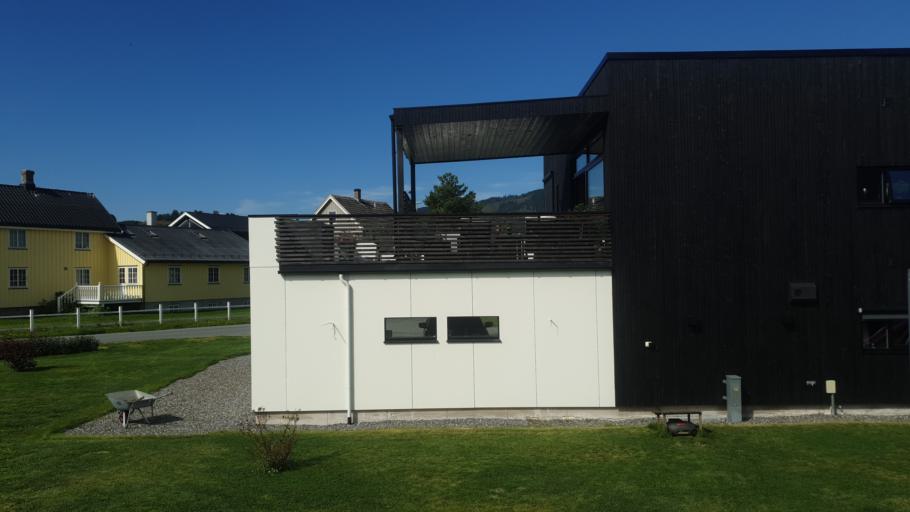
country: NO
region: Sor-Trondelag
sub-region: Orkdal
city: Orkanger
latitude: 63.2750
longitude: 9.8229
